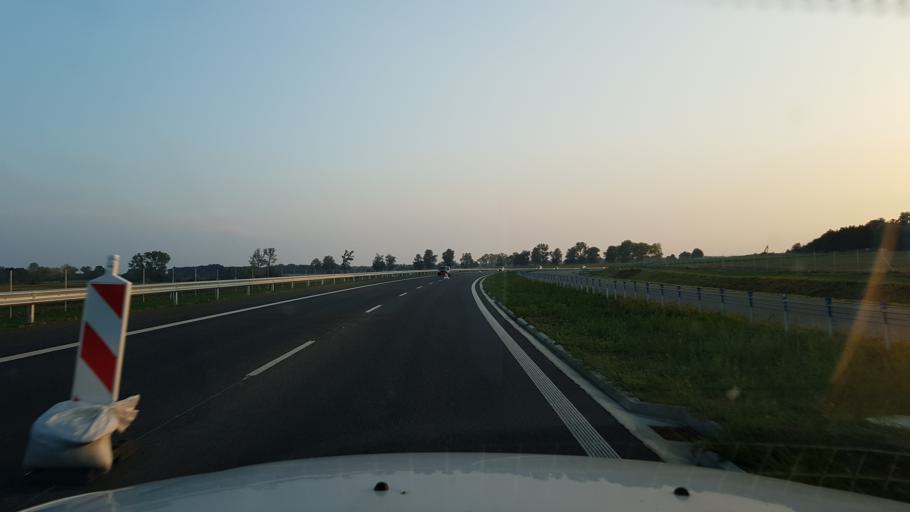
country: PL
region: West Pomeranian Voivodeship
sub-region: Powiat goleniowski
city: Nowogard
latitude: 53.7176
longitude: 15.1937
